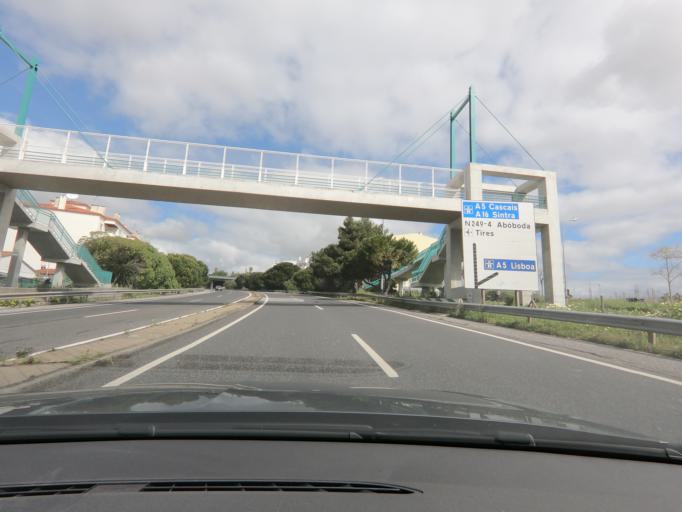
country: PT
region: Lisbon
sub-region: Cascais
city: Sao Domingos de Rana
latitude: 38.7037
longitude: -9.3341
